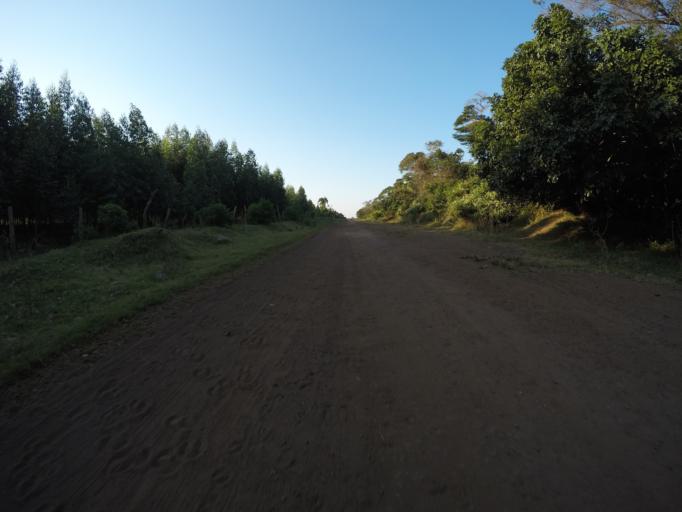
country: ZA
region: KwaZulu-Natal
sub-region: uThungulu District Municipality
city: KwaMbonambi
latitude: -28.6969
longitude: 32.1955
